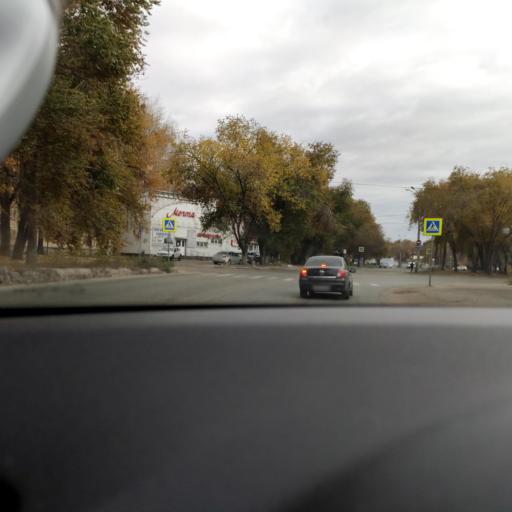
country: RU
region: Samara
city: Smyshlyayevka
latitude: 53.2257
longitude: 50.2902
